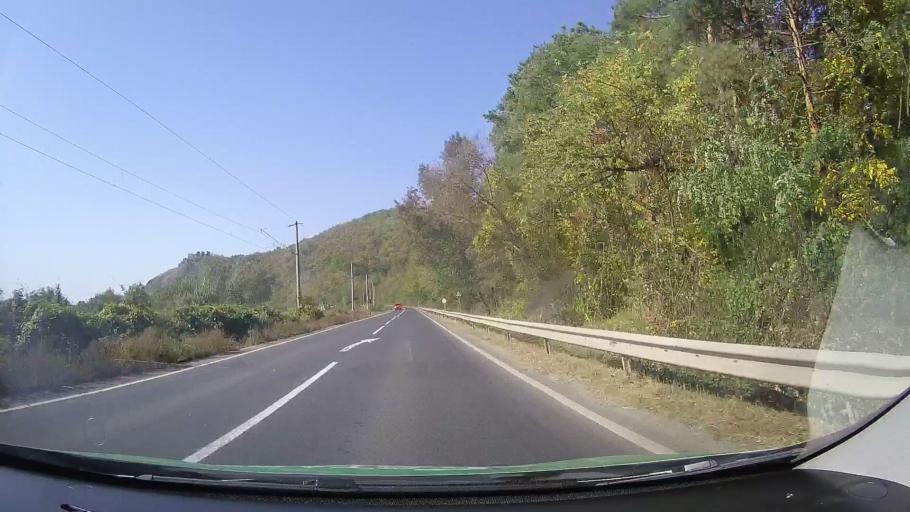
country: RO
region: Arad
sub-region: Oras Lipova
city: Lipova
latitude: 46.1079
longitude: 21.7373
